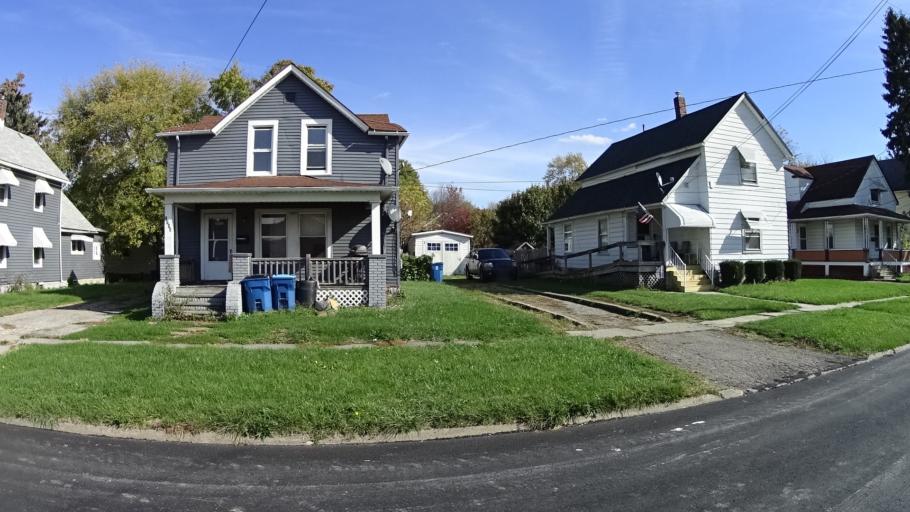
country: US
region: Ohio
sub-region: Lorain County
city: Lorain
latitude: 41.4548
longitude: -82.1735
